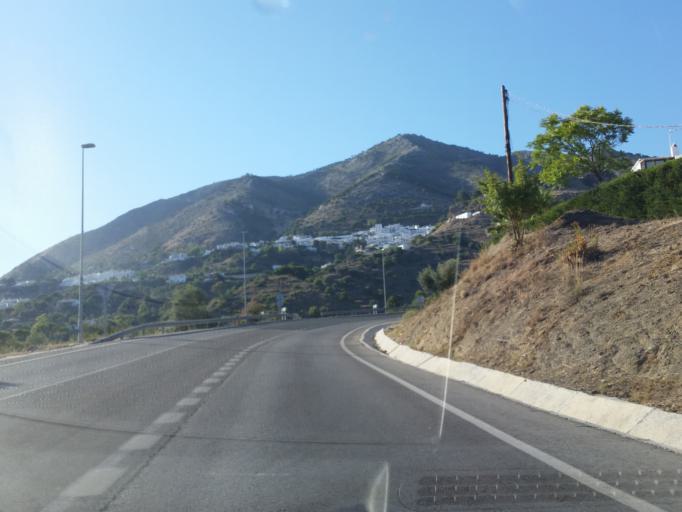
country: ES
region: Andalusia
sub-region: Provincia de Malaga
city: Mijas
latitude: 36.5857
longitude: -4.6371
